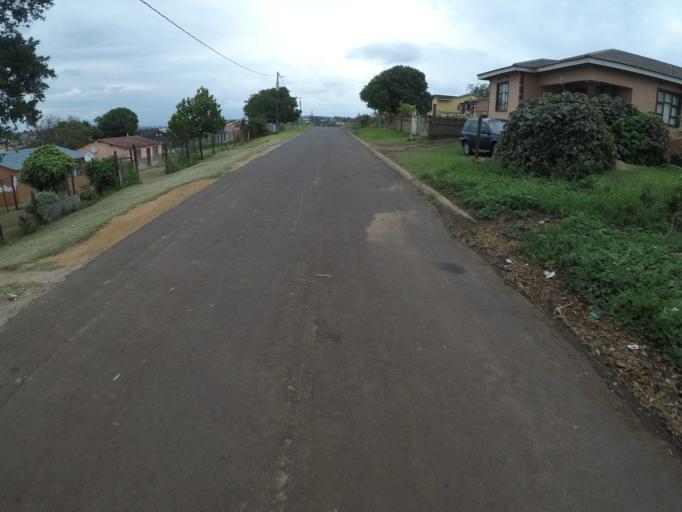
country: ZA
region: KwaZulu-Natal
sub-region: uThungulu District Municipality
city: Empangeni
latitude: -28.7746
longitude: 31.8562
